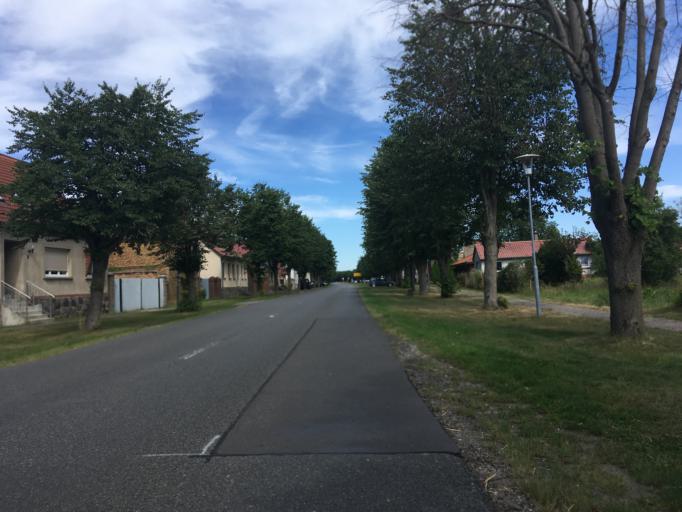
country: DE
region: Brandenburg
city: Lindow
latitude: 53.0226
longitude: 12.9690
